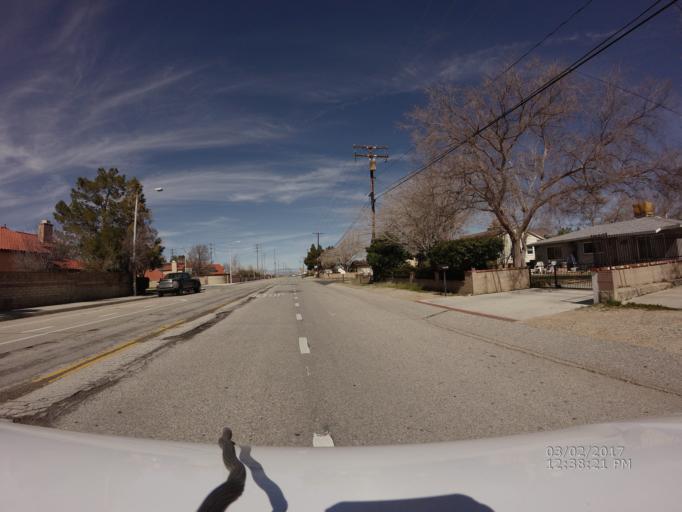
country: US
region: California
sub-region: Los Angeles County
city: Quartz Hill
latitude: 34.6580
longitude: -118.2275
